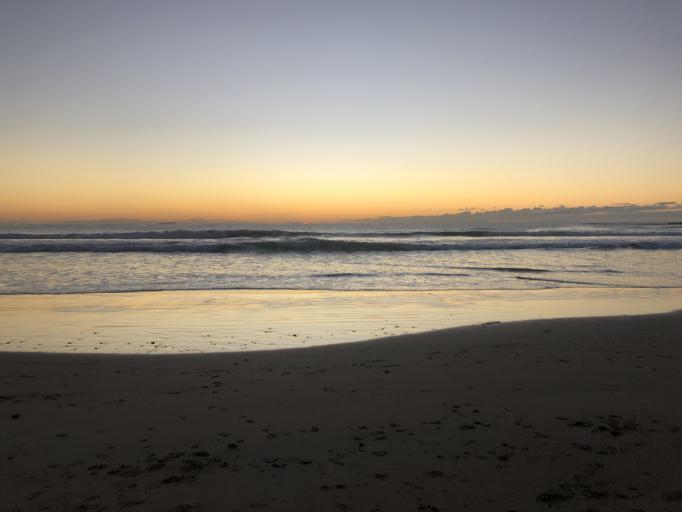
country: AU
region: New South Wales
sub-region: Coffs Harbour
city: Coffs Harbour
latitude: -30.3012
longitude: 153.1406
